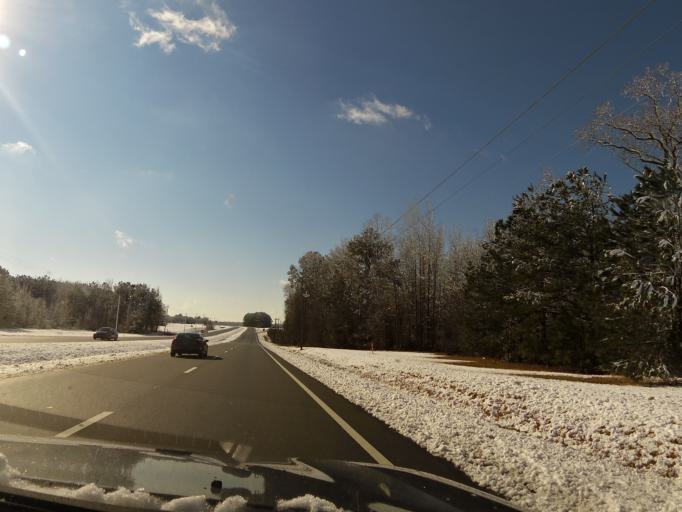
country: US
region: North Carolina
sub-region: Wilson County
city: Elm City
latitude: 35.8326
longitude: -77.8557
